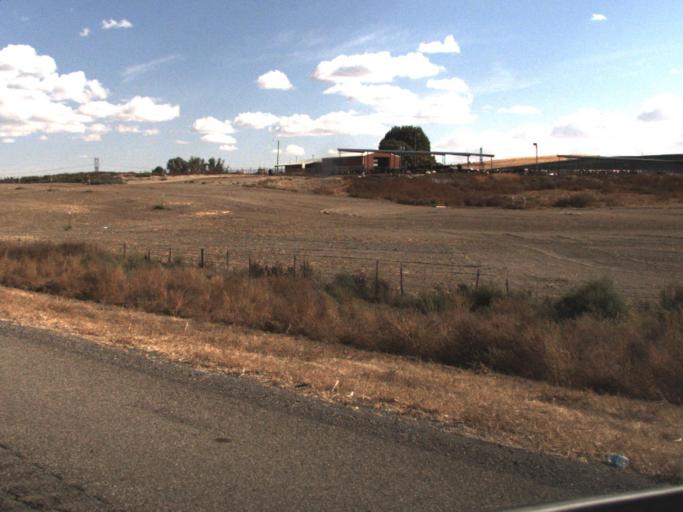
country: US
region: Washington
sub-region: Yakima County
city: Granger
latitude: 46.3382
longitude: -120.1514
